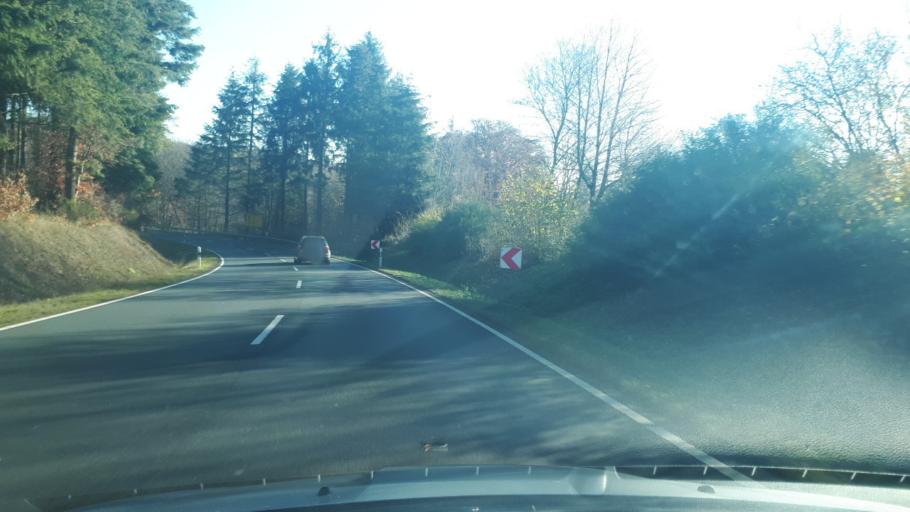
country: DE
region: Rheinland-Pfalz
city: Buchel
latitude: 50.1617
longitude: 7.1006
